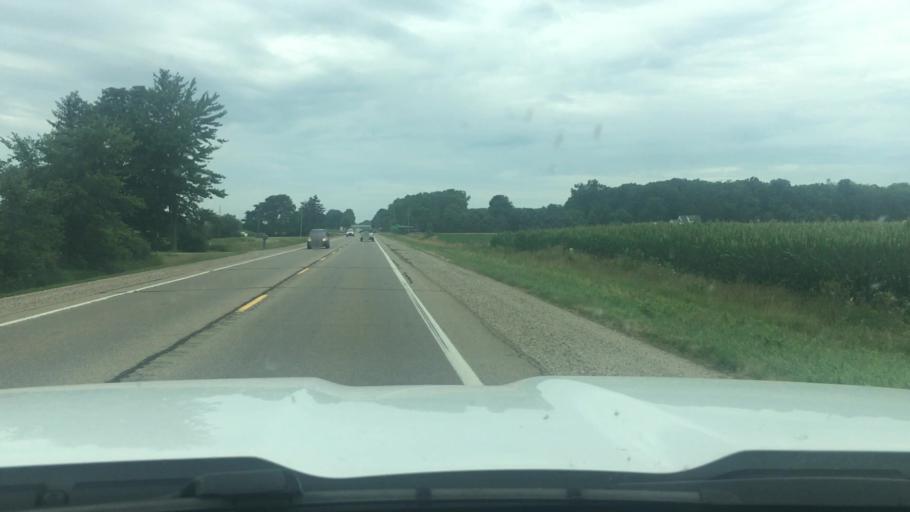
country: US
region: Michigan
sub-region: Clinton County
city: Saint Johns
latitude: 43.0013
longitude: -84.4976
